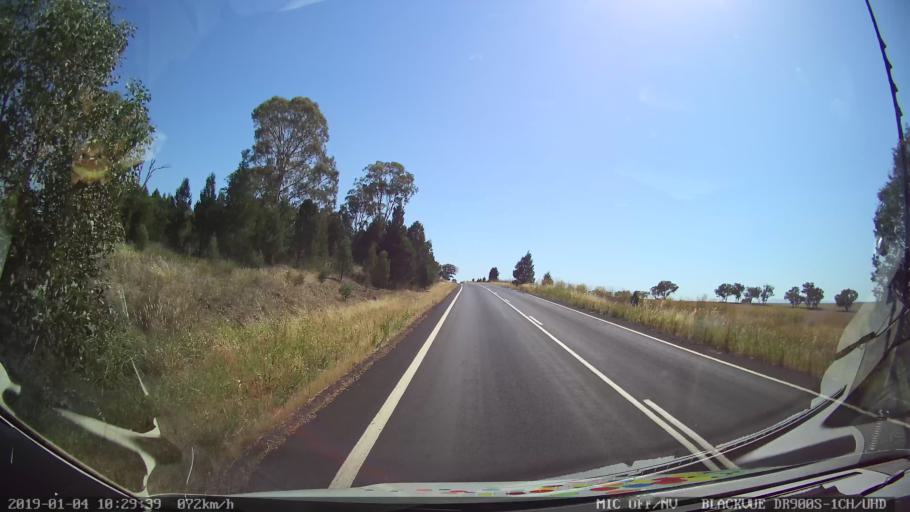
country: AU
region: New South Wales
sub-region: Cabonne
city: Canowindra
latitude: -33.3539
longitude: 148.6222
